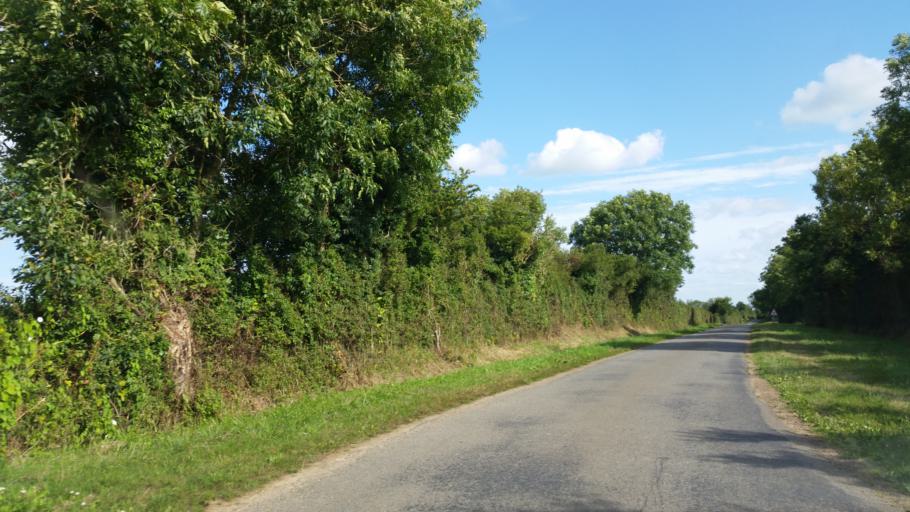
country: FR
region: Lower Normandy
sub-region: Departement de la Manche
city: Sainte-Mere-Eglise
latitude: 49.4631
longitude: -1.3029
